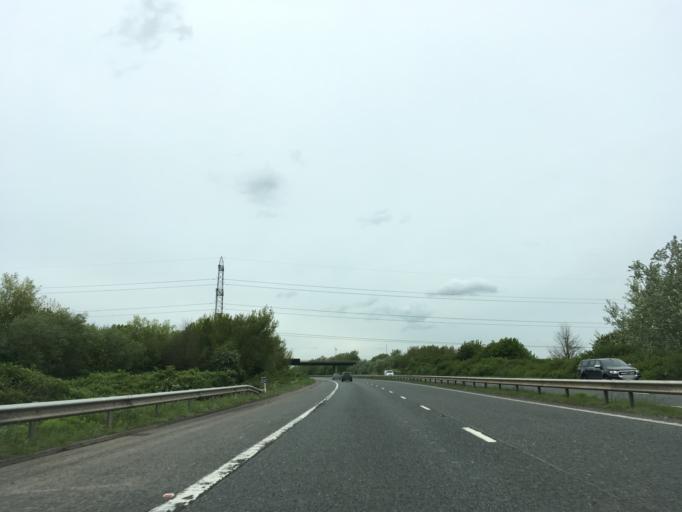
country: GB
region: England
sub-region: South Gloucestershire
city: Severn Beach
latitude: 51.5485
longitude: -2.6396
